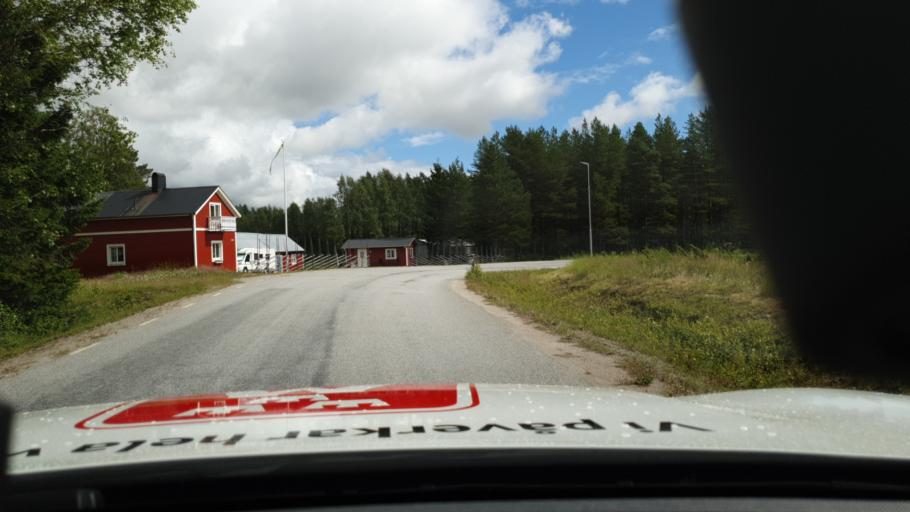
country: SE
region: Norrbotten
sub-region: Pitea Kommun
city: Rosvik
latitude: 65.4155
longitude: 21.7536
